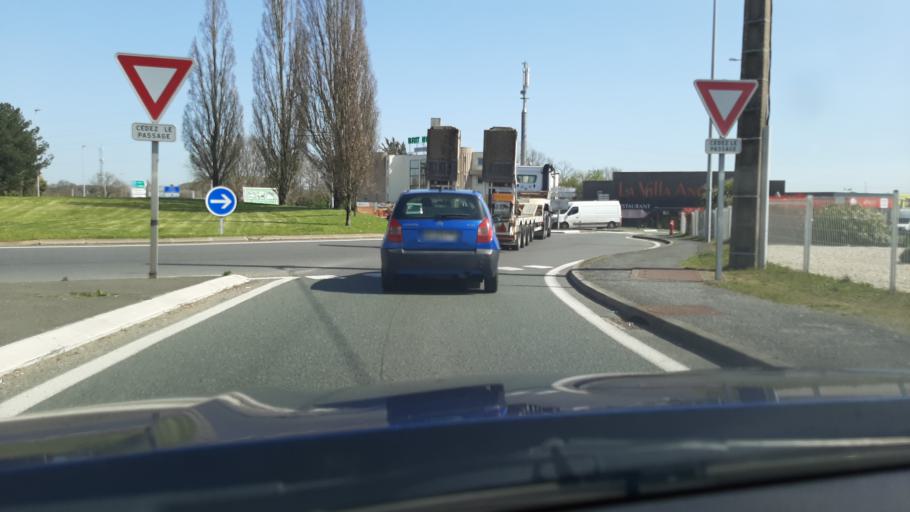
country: FR
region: Pays de la Loire
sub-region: Departement de Maine-et-Loire
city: Ecouflant
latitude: 47.4973
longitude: -0.4930
